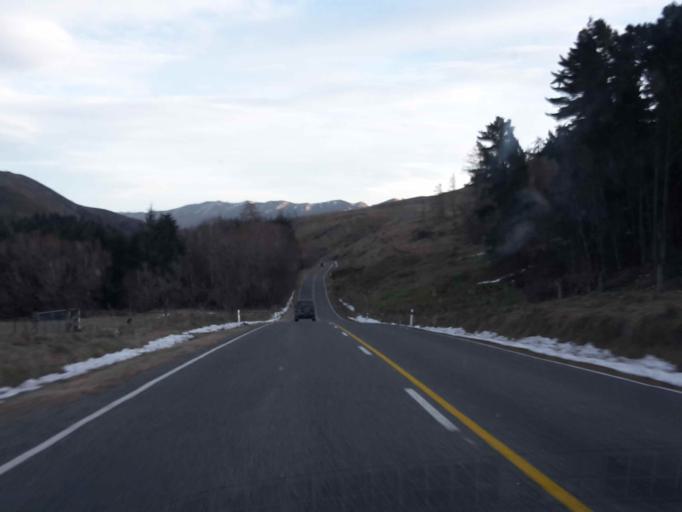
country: NZ
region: Canterbury
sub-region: Timaru District
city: Pleasant Point
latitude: -44.0510
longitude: 170.6797
